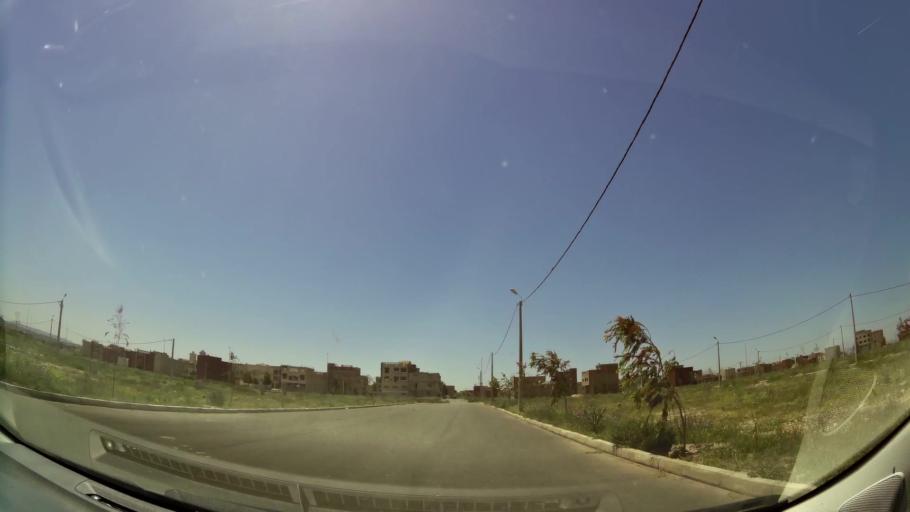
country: MA
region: Oriental
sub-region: Oujda-Angad
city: Oujda
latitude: 34.6829
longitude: -1.8615
